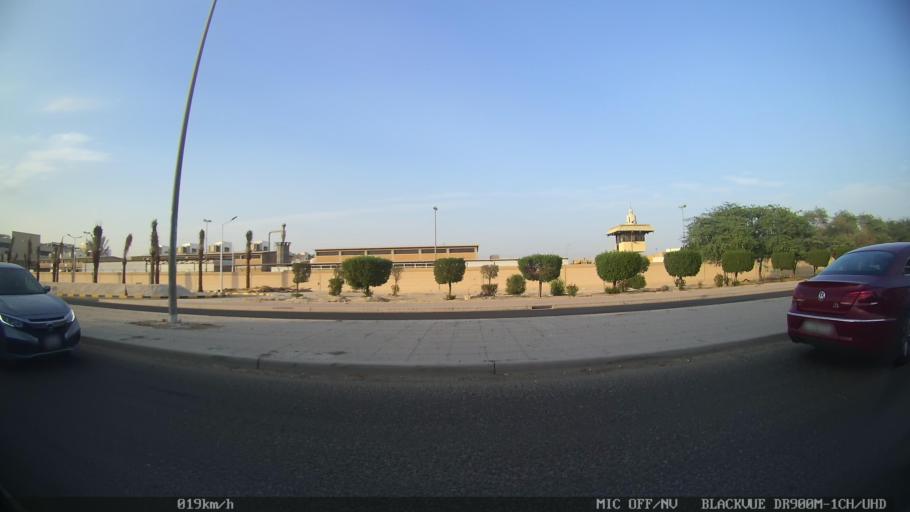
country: KW
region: Al Farwaniyah
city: Janub as Surrah
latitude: 29.2569
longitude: 48.0149
